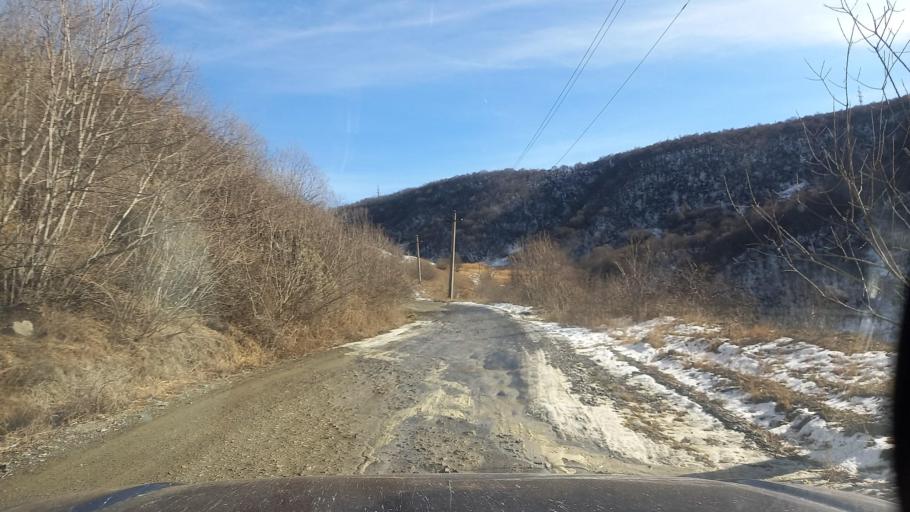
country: RU
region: North Ossetia
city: Verkhniy Fiagdon
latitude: 42.8362
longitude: 44.4699
